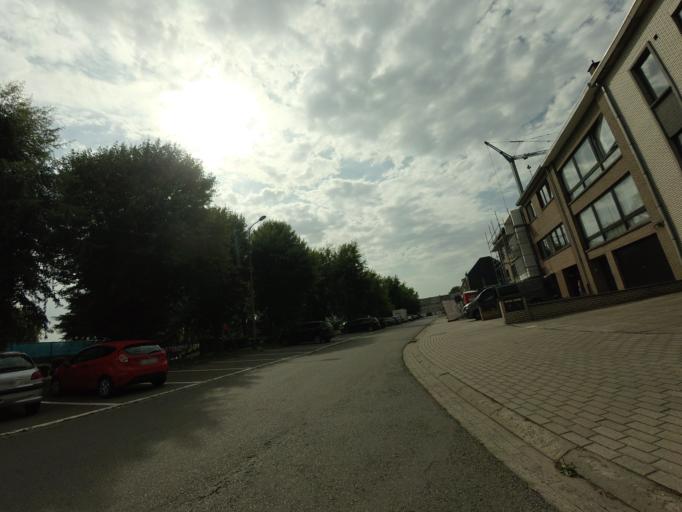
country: BE
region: Flanders
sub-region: Provincie Vlaams-Brabant
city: Grimbergen
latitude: 50.9127
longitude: 4.3539
